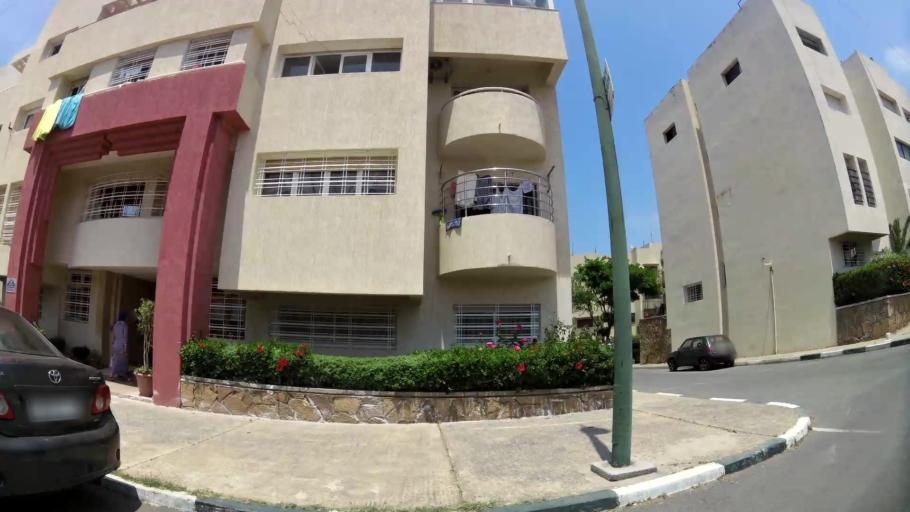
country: MA
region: Rabat-Sale-Zemmour-Zaer
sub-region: Skhirate-Temara
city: Temara
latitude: 33.9663
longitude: -6.9061
